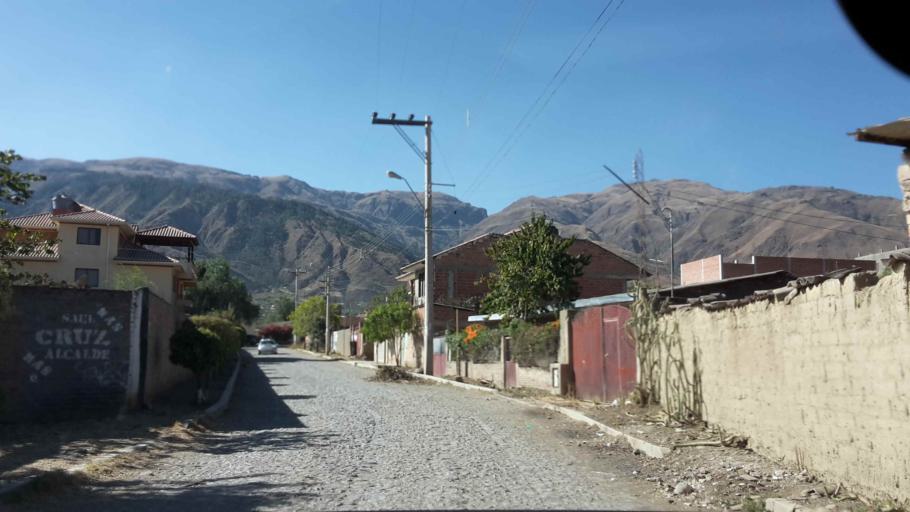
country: BO
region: Cochabamba
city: Cochabamba
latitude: -17.3363
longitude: -66.2218
